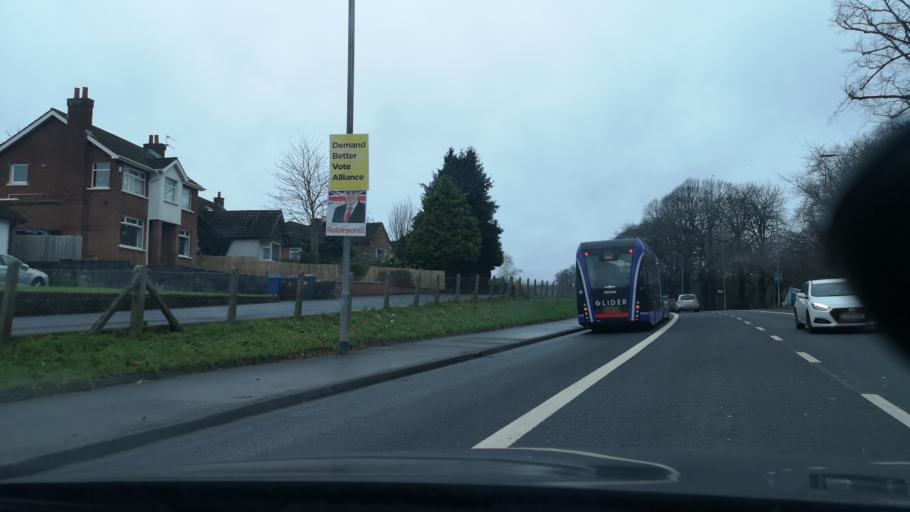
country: GB
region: Northern Ireland
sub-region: Castlereagh District
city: Dundonald
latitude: 54.5947
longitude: -5.8286
